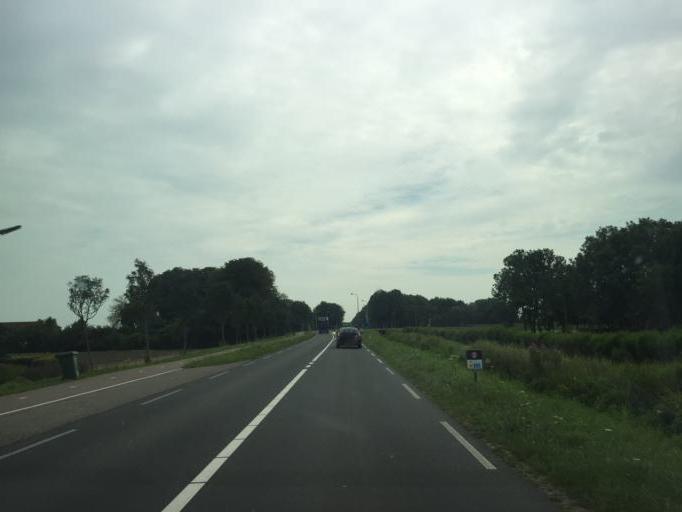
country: NL
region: North Holland
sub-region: Gemeente Alkmaar
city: Alkmaar
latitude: 52.6174
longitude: 4.7931
